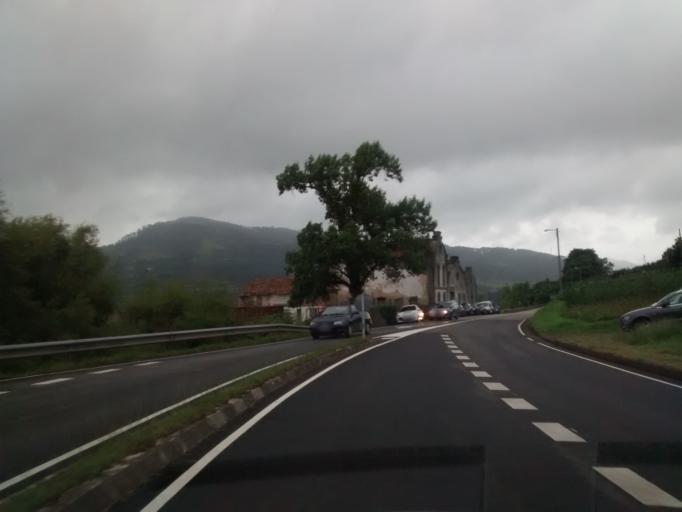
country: ES
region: Asturias
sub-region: Province of Asturias
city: Villaviciosa
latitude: 43.5006
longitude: -5.4267
